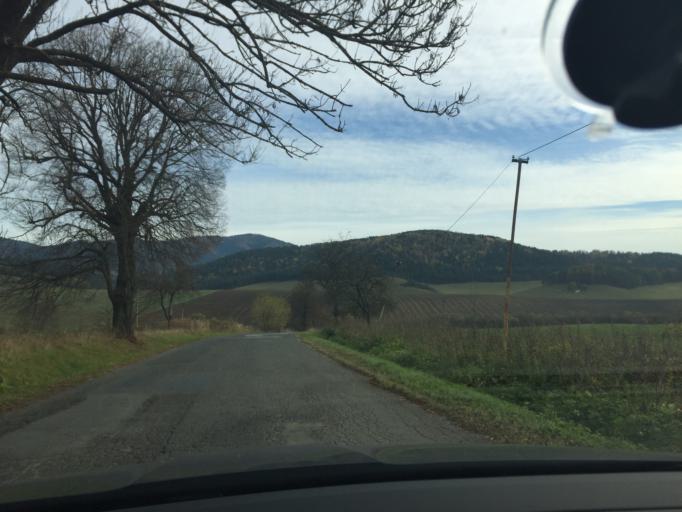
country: SK
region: Presovsky
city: Spisske Podhradie
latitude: 48.9883
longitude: 20.7901
